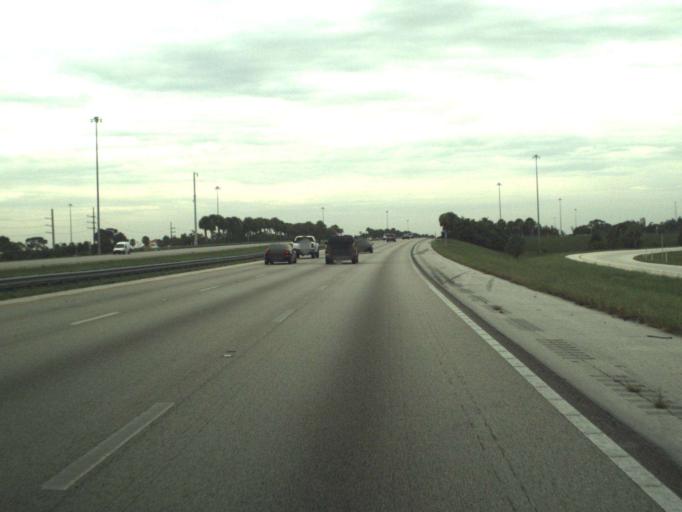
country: US
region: Florida
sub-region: Martin County
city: Palm City
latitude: 27.1129
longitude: -80.2633
